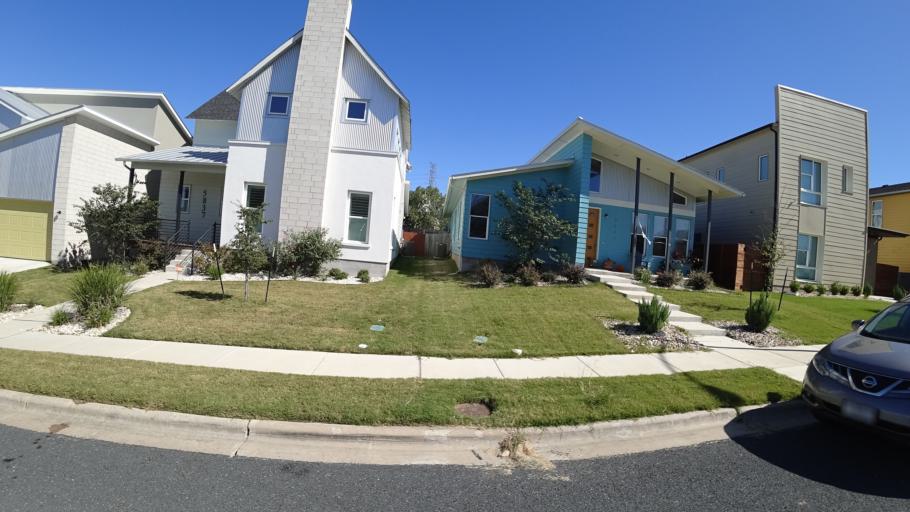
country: US
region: Texas
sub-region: Travis County
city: Hornsby Bend
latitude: 30.2897
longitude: -97.6437
